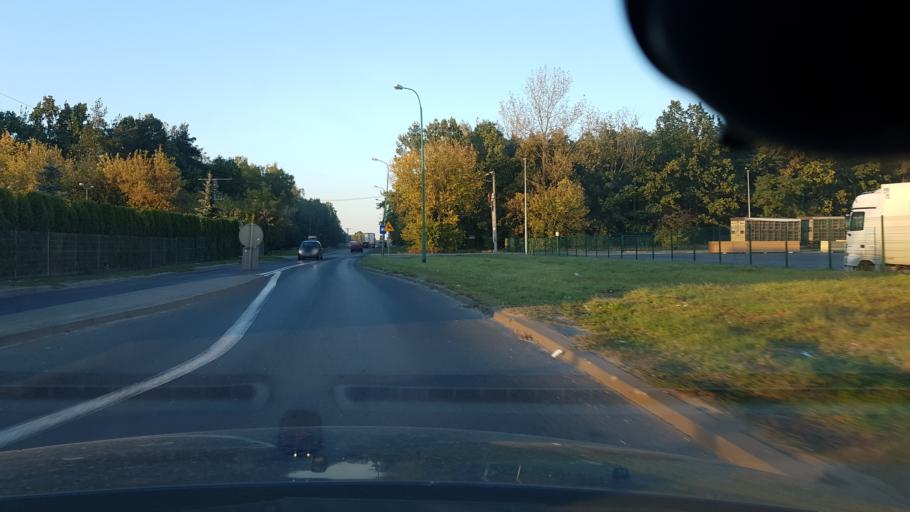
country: PL
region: Lodz Voivodeship
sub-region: Powiat tomaszowski
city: Tomaszow Mazowiecki
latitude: 51.5593
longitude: 20.0203
